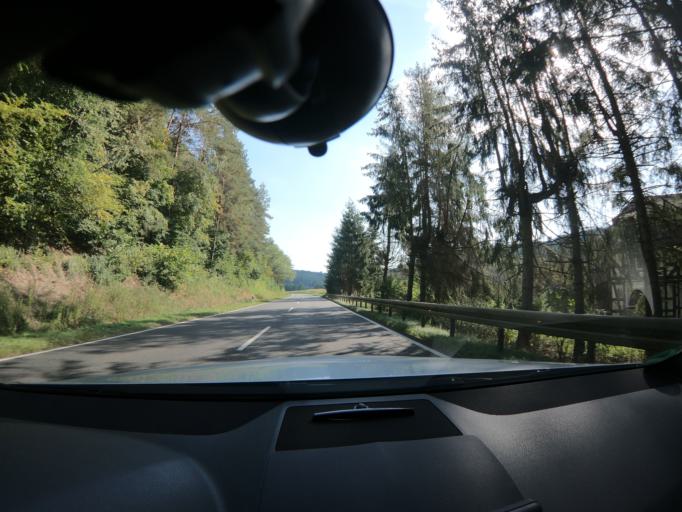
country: DE
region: Hesse
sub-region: Regierungsbezirk Giessen
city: Rauschenberg
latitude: 50.8604
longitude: 8.9311
